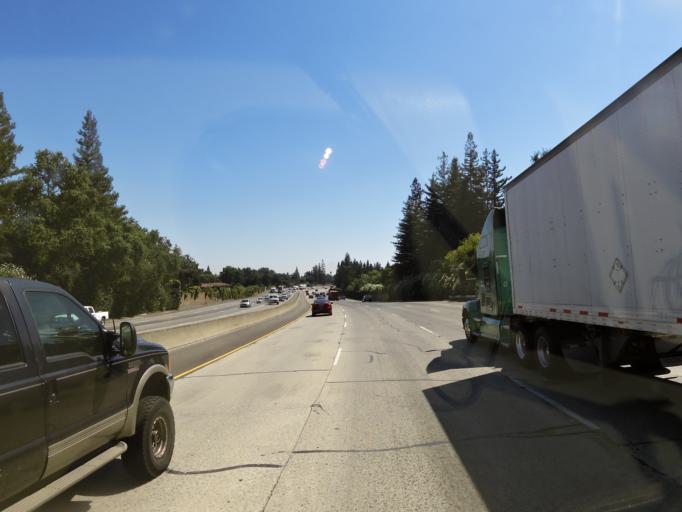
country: US
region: California
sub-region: Yolo County
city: West Sacramento
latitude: 38.5339
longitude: -121.5173
